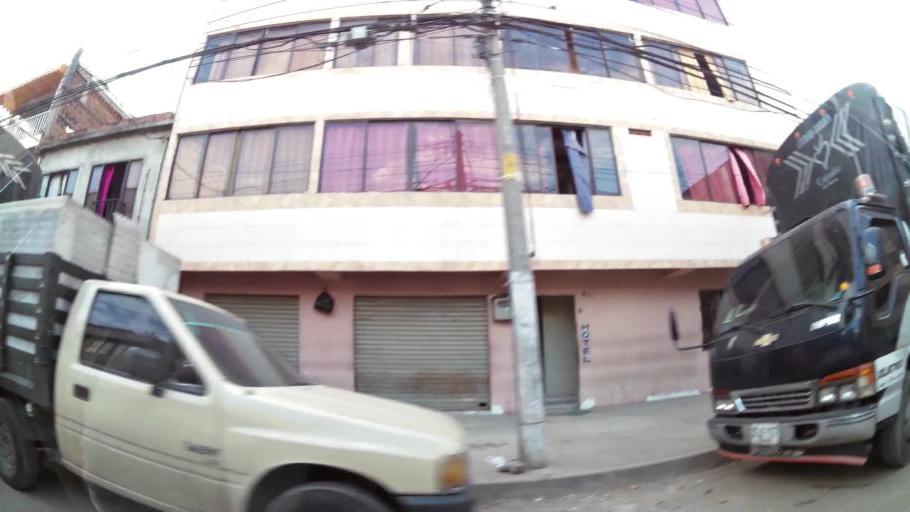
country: CO
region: Valle del Cauca
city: Cali
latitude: 3.4628
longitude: -76.5139
